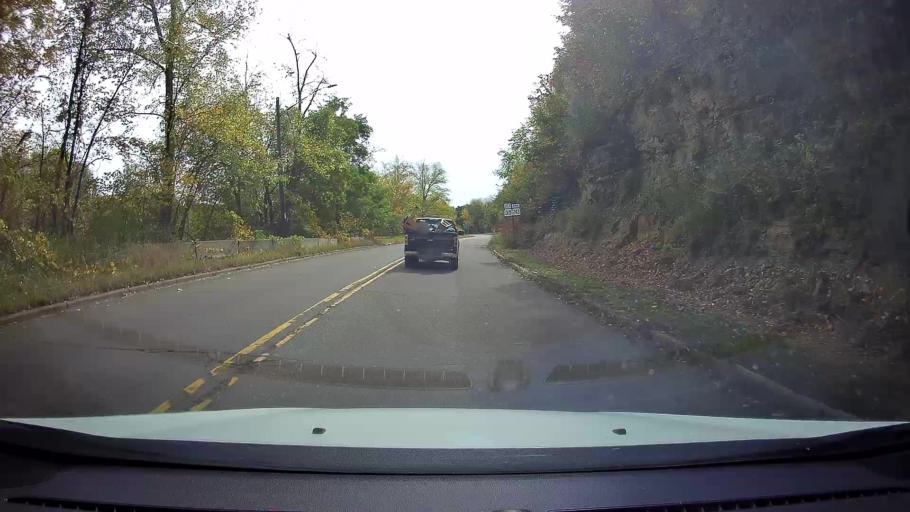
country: US
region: Wisconsin
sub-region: Polk County
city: Osceola
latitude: 45.3202
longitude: -92.7081
